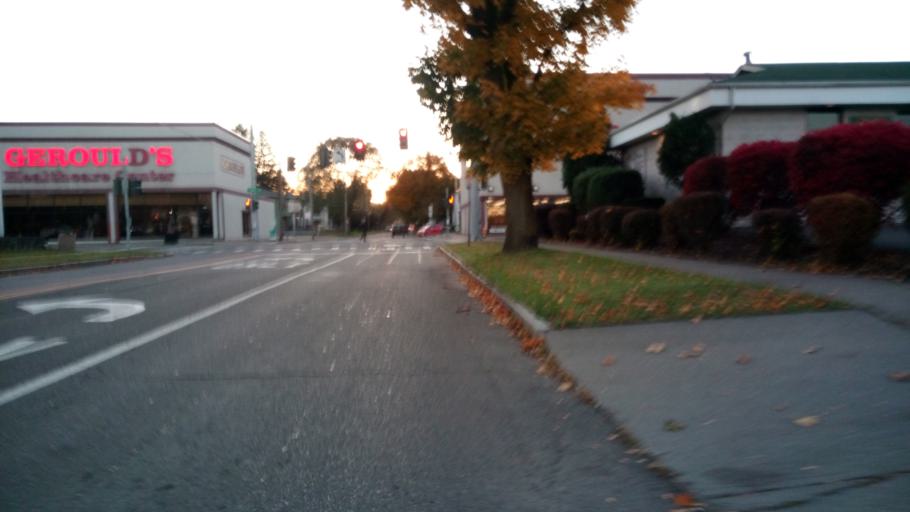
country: US
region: New York
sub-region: Chemung County
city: Elmira
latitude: 42.0836
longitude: -76.8048
